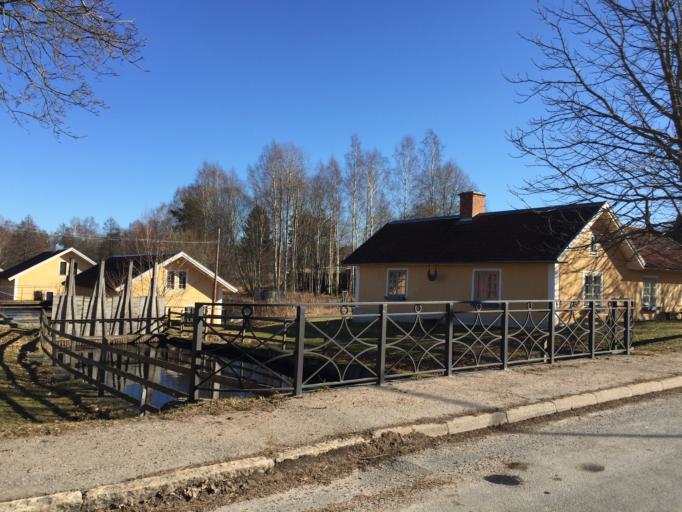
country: SE
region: OErebro
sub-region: Orebro Kommun
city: Odensbacken
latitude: 59.0116
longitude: 15.5823
